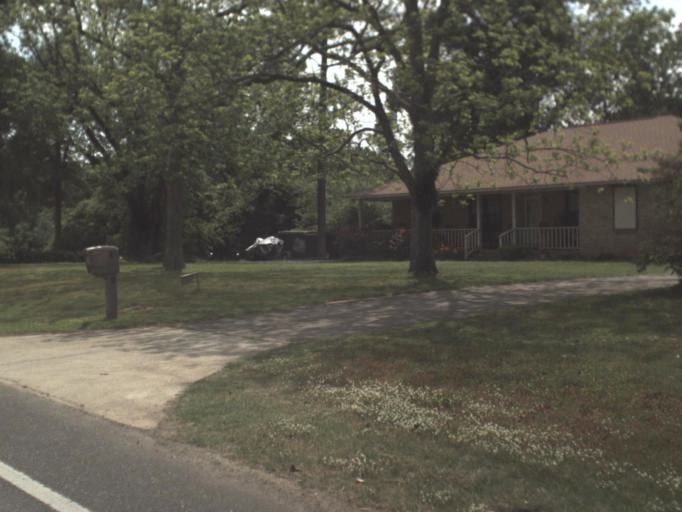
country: US
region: Alabama
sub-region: Escambia County
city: East Brewton
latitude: 30.9849
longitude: -87.1160
